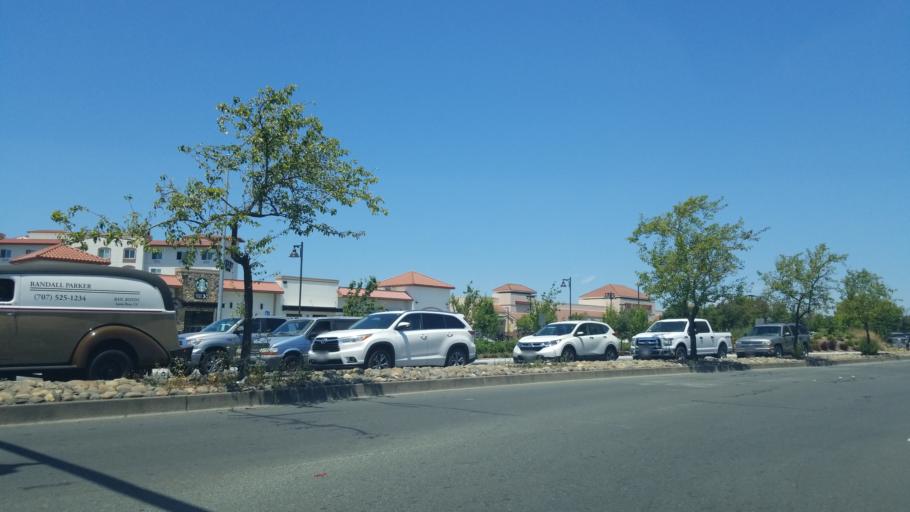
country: US
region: California
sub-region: Sonoma County
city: Rohnert Park
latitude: 38.3634
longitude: -122.7150
